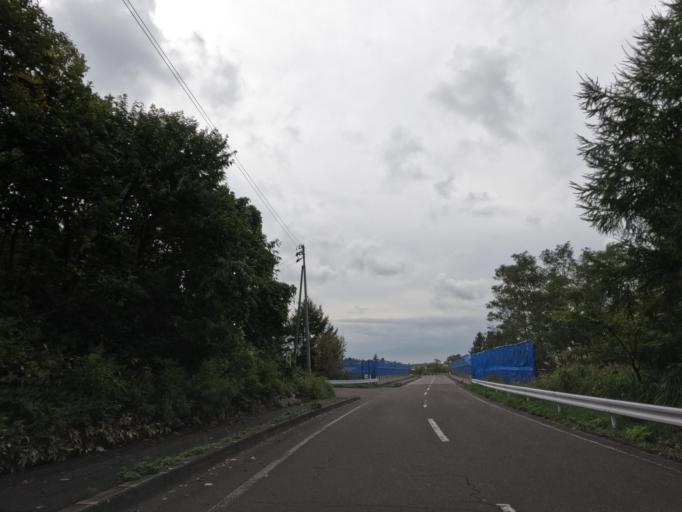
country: JP
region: Hokkaido
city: Date
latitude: 42.4711
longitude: 140.9069
